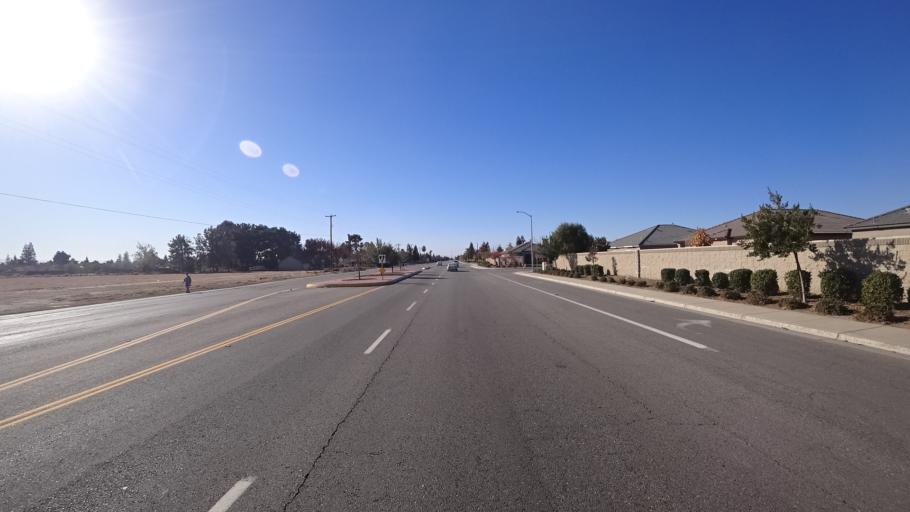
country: US
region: California
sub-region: Kern County
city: Greenfield
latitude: 35.2815
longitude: -119.0399
